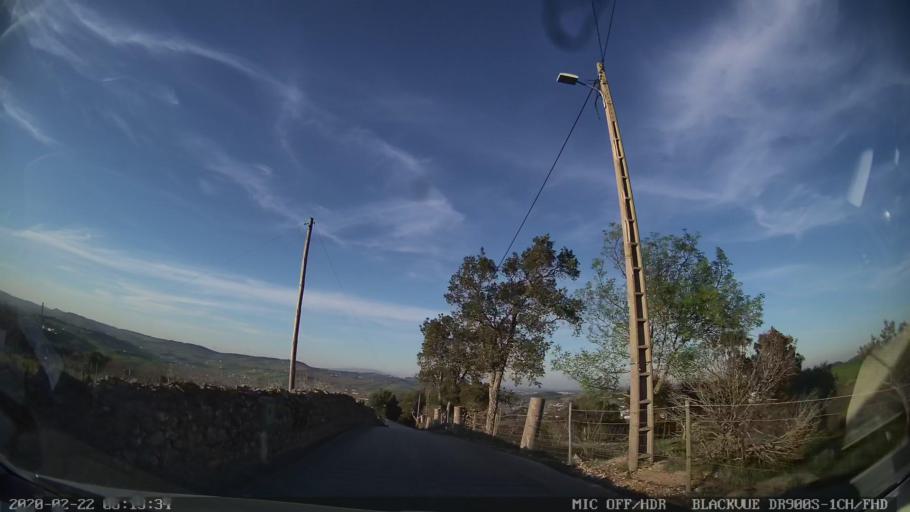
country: PT
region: Lisbon
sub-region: Vila Franca de Xira
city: Vila Franca de Xira
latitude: 38.9800
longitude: -9.0148
